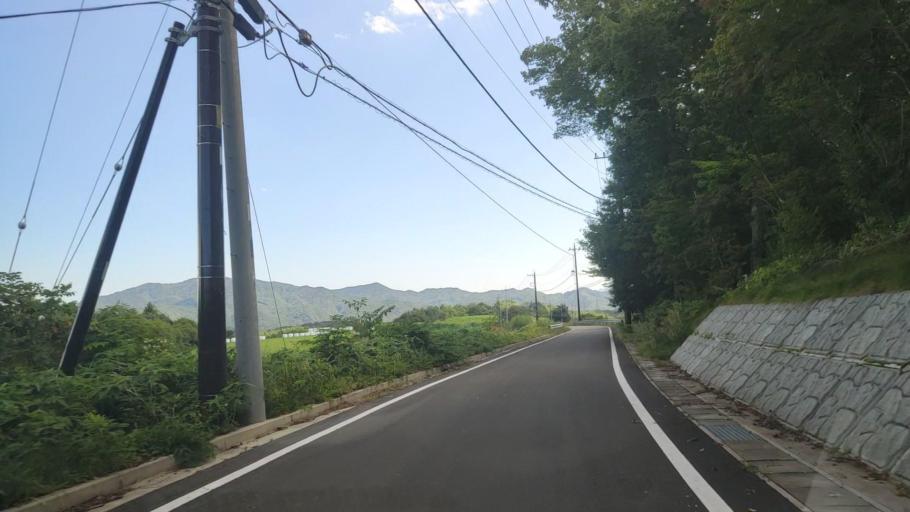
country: JP
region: Gunma
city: Nakanojomachi
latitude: 36.6446
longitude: 138.6156
